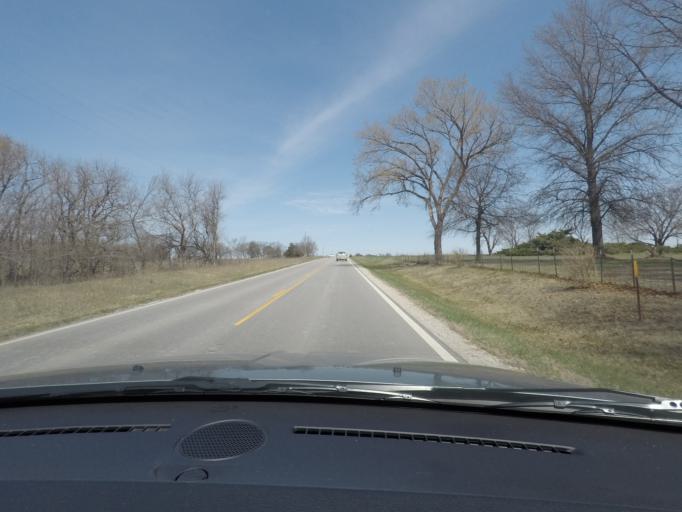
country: US
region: Kansas
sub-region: Lyon County
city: Emporia
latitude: 38.4886
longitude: -96.1709
